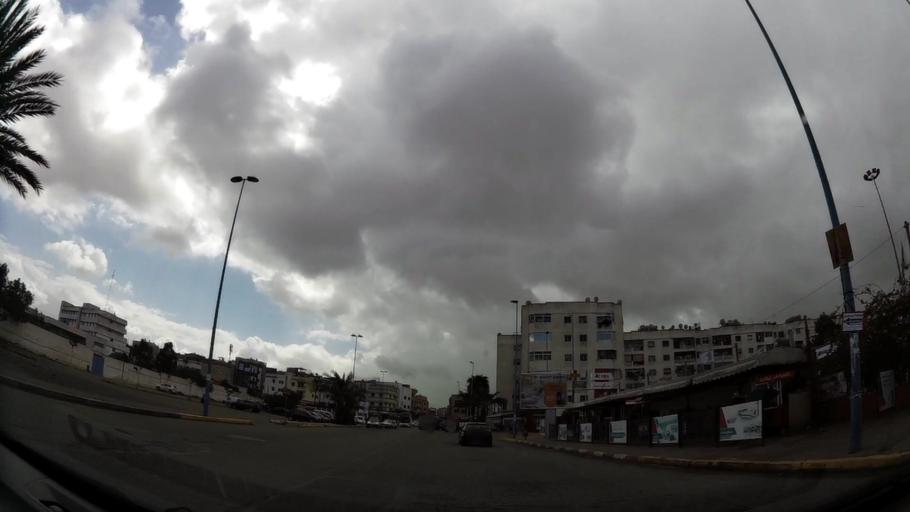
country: MA
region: Grand Casablanca
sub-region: Casablanca
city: Casablanca
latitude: 33.5404
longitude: -7.6002
